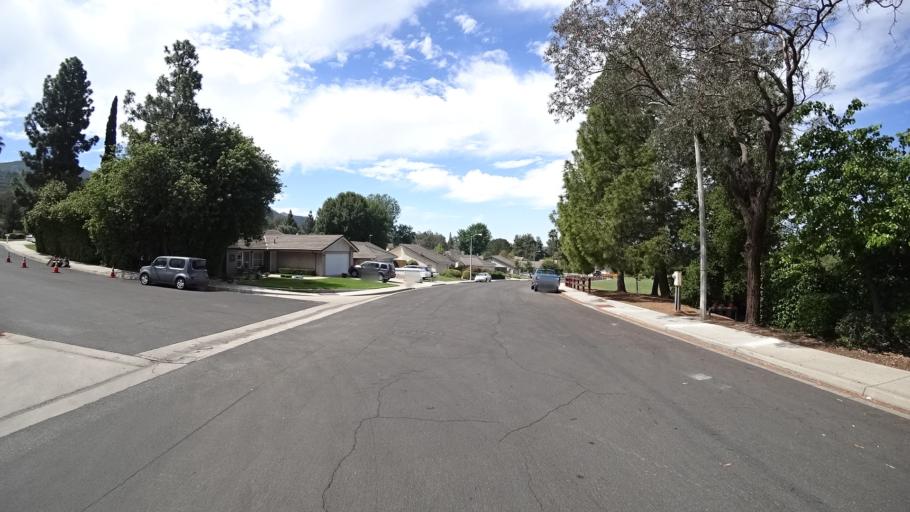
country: US
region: California
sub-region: Ventura County
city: Casa Conejo
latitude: 34.1629
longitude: -118.9415
